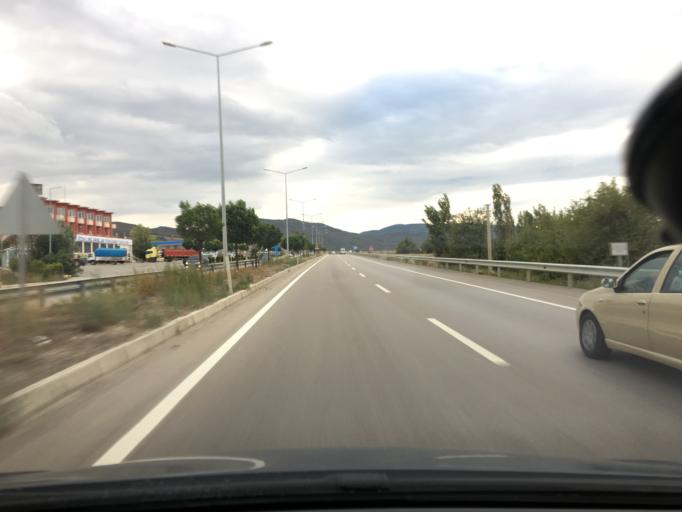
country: TR
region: Afyonkarahisar
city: Sincanli
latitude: 38.7252
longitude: 30.3406
